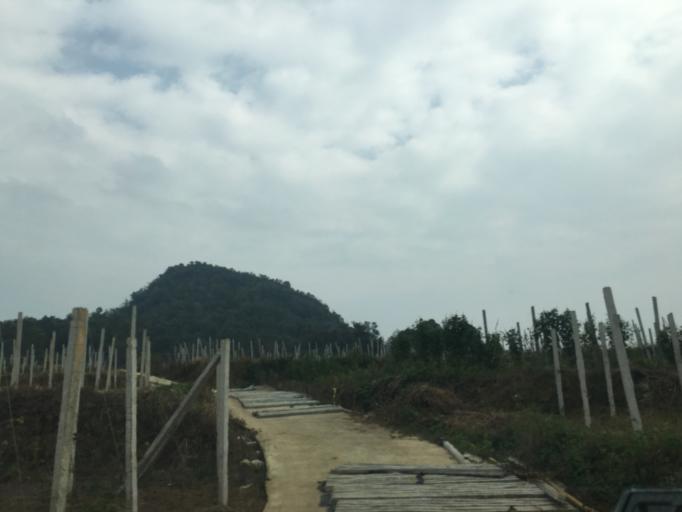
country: CN
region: Guangxi Zhuangzu Zizhiqu
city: Xinzhou
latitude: 25.4864
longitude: 105.6514
